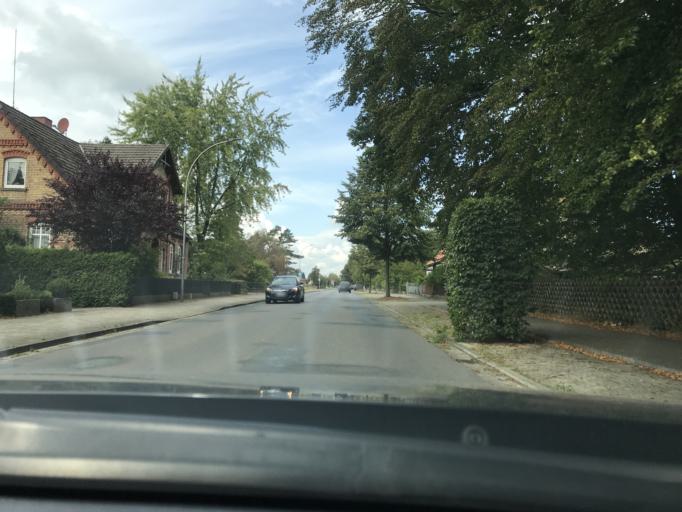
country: DE
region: Lower Saxony
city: Suderburg
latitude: 52.8958
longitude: 10.4434
